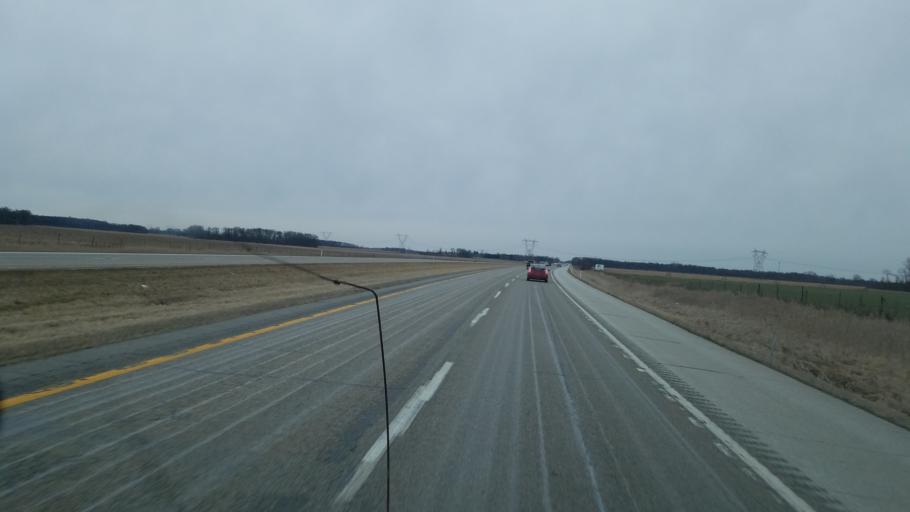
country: US
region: Indiana
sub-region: LaPorte County
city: Wanatah
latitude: 41.4306
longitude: -86.8078
